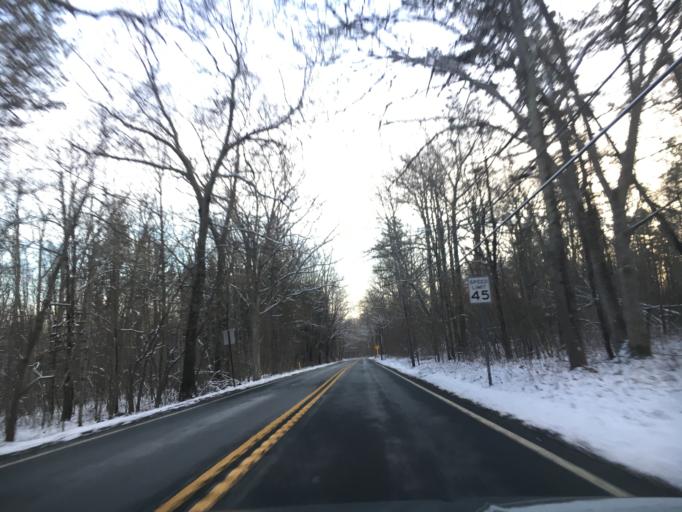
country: US
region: Pennsylvania
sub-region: Pike County
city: Saw Creek
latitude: 41.1634
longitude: -75.0837
